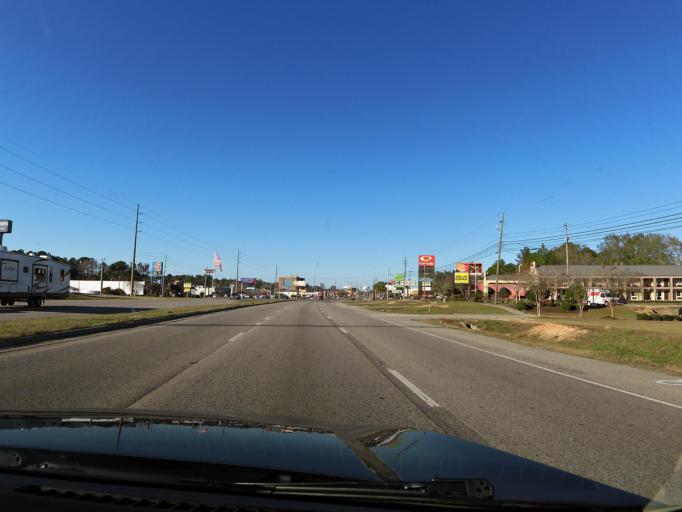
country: US
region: Alabama
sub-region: Houston County
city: Dothan
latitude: 31.2163
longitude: -85.4308
